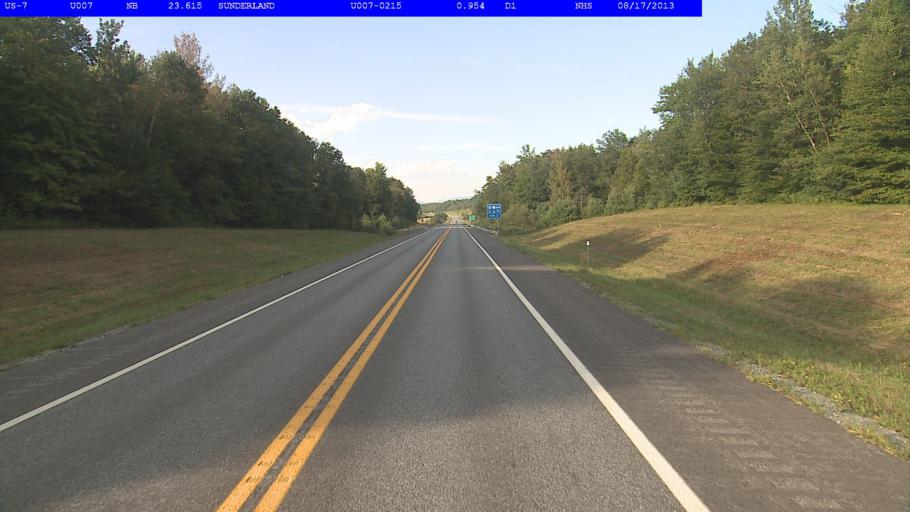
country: US
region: Vermont
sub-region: Bennington County
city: Arlington
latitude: 43.0388
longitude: -73.1343
